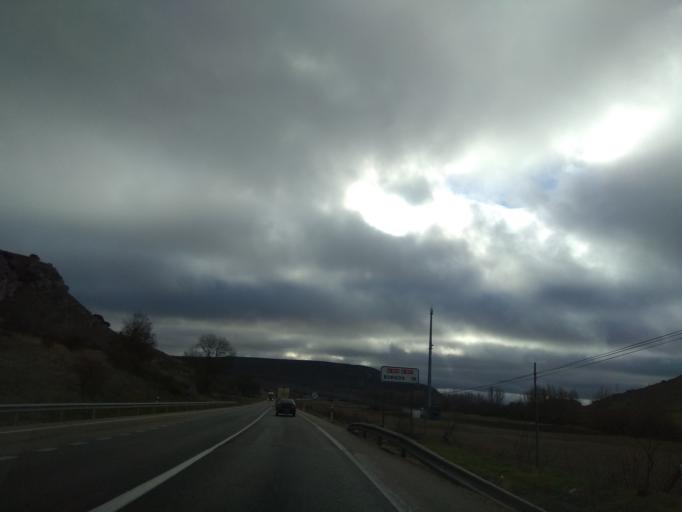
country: ES
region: Castille and Leon
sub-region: Provincia de Burgos
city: Quintanaortuno
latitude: 42.5039
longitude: -3.7033
